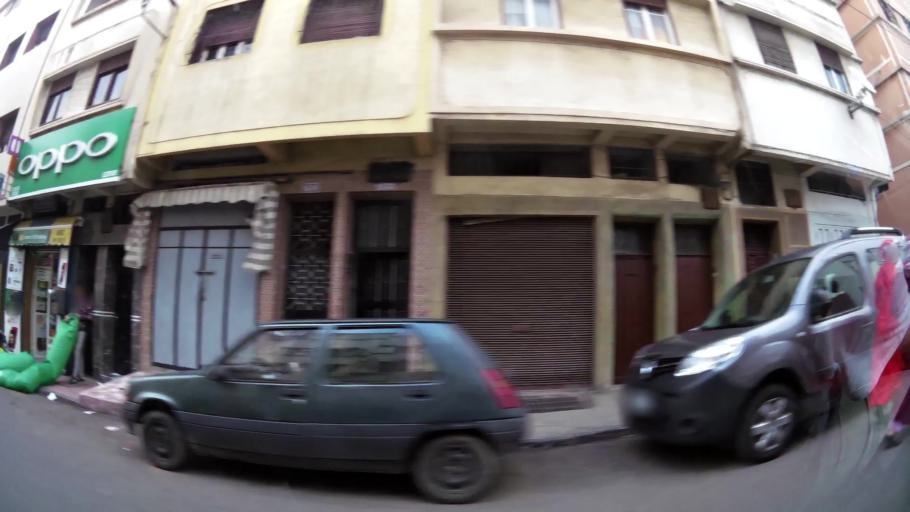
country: MA
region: Grand Casablanca
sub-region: Casablanca
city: Casablanca
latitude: 33.5569
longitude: -7.5976
